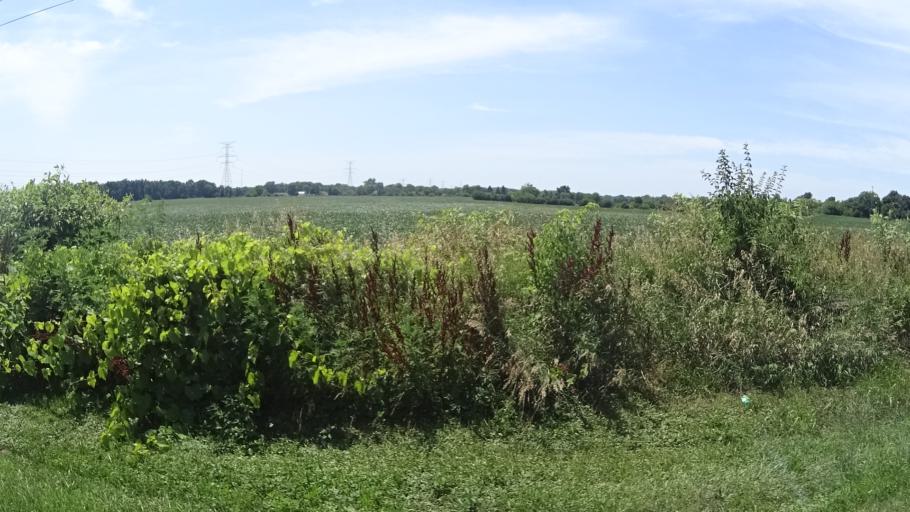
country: US
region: Ohio
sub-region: Erie County
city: Sandusky
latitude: 41.3886
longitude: -82.7876
